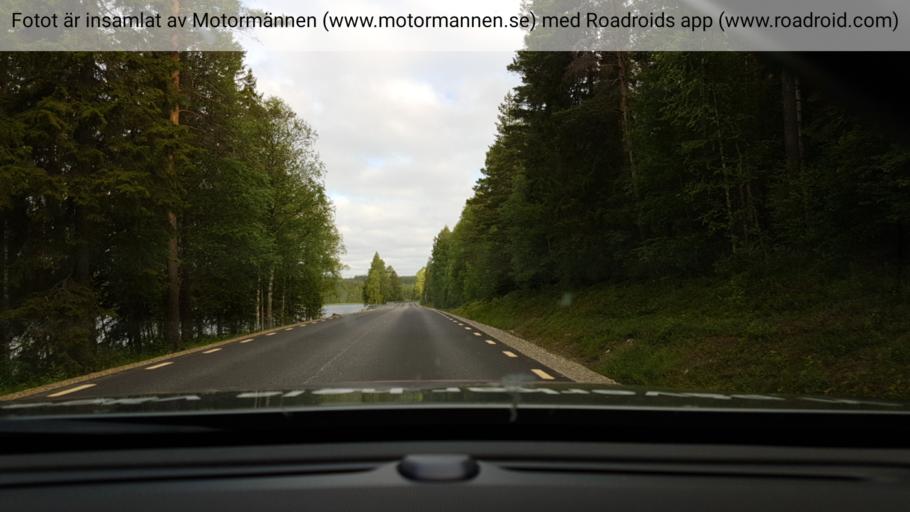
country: SE
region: Vaesterbotten
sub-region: Vindelns Kommun
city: Vindeln
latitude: 64.4404
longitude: 19.3453
